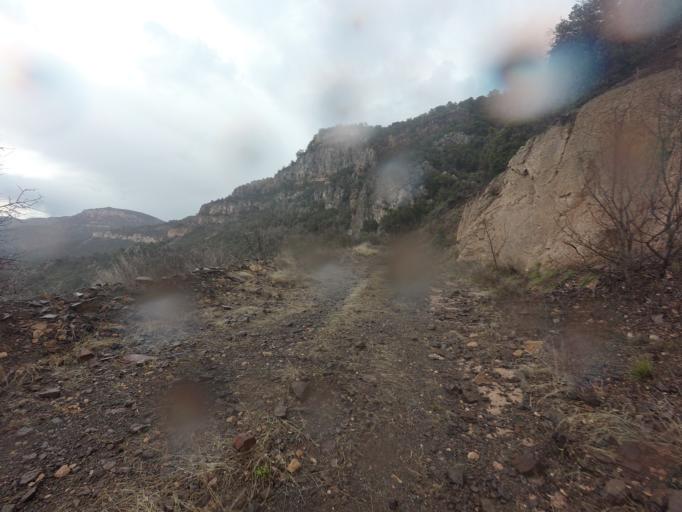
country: US
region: Arizona
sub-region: Gila County
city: Pine
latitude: 34.4082
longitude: -111.5882
